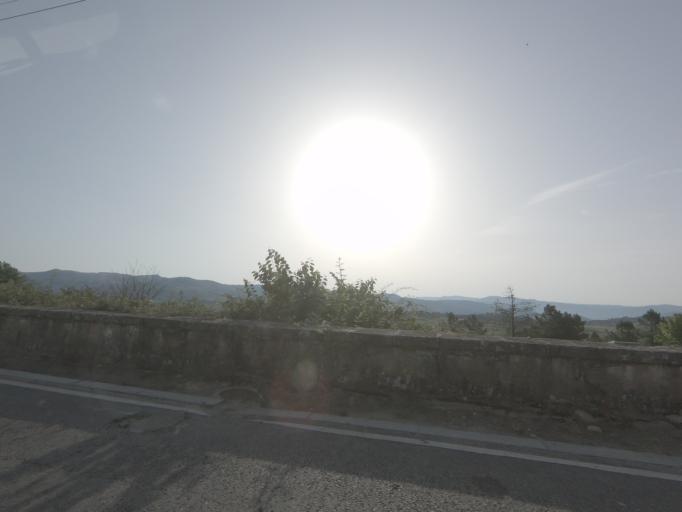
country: PT
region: Vila Real
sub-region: Sabrosa
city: Sabrosa
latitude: 41.2660
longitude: -7.4748
